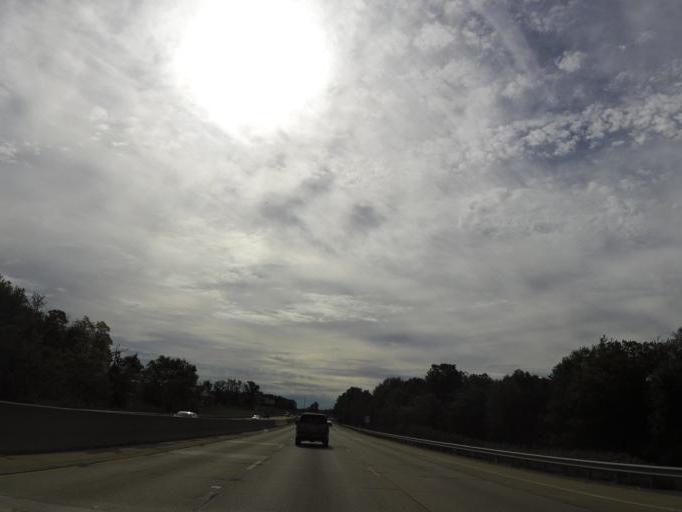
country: US
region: Ohio
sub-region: Summit County
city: Silver Lake
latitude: 41.1972
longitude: -81.4806
